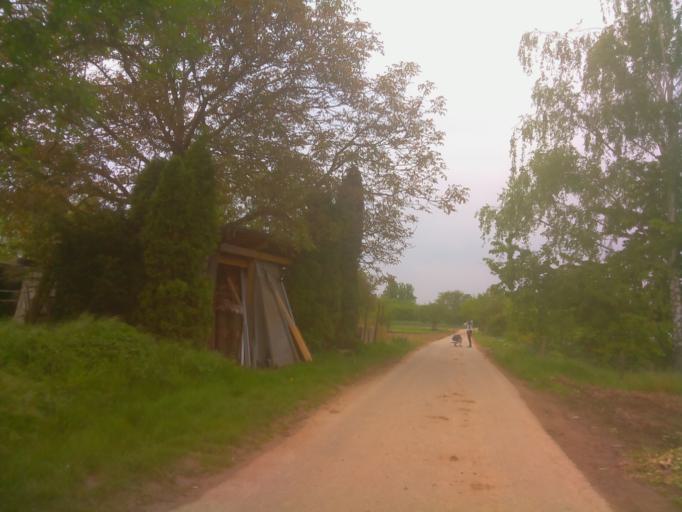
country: DE
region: Baden-Wuerttemberg
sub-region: Karlsruhe Region
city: Dossenheim
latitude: 49.4384
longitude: 8.6706
